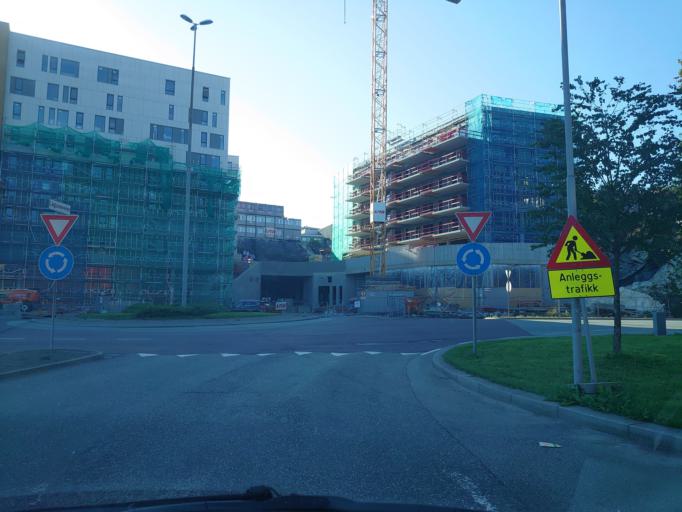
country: NO
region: Hordaland
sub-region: Bergen
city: Sandsli
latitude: 60.2968
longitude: 5.3280
